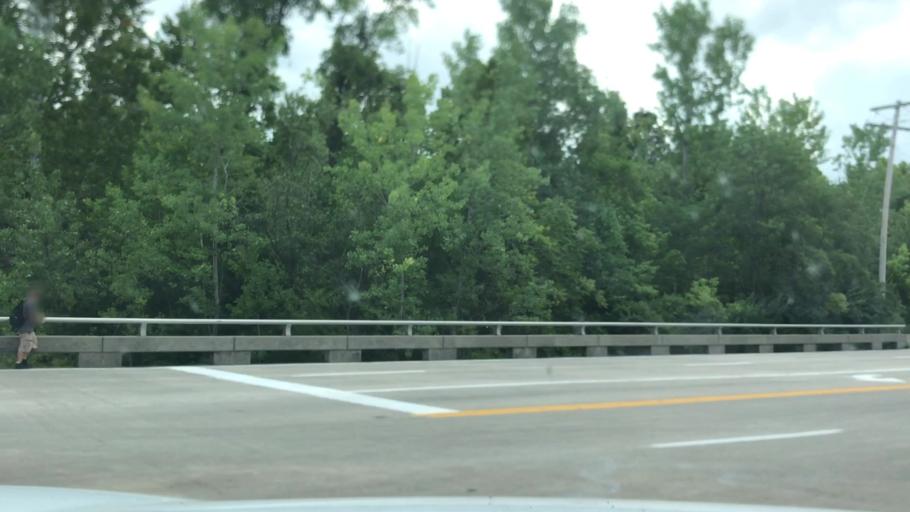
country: US
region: Missouri
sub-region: Saint Charles County
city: O'Fallon
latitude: 38.7916
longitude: -90.7017
